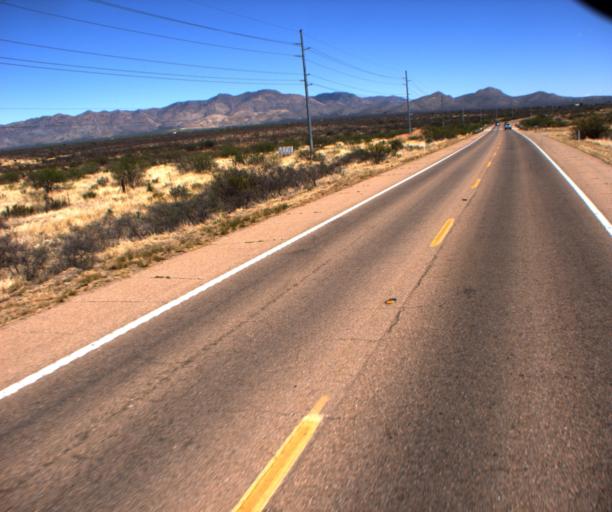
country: US
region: Arizona
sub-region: Cochise County
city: Naco
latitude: 31.3803
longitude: -110.0748
